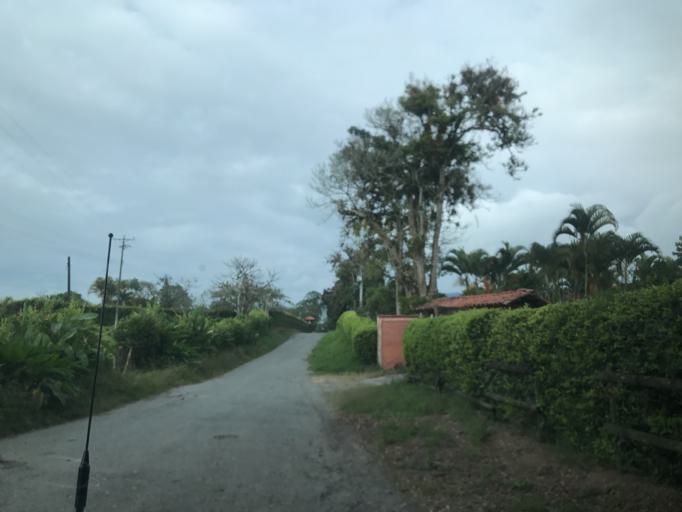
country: CO
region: Quindio
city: Montenegro
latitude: 4.5409
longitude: -75.8561
